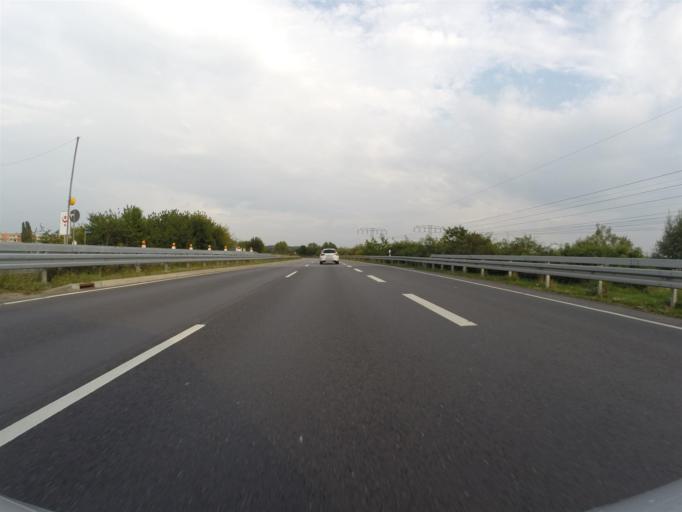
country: DE
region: Saxony-Anhalt
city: Angersdorf
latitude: 51.4659
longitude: 11.9184
